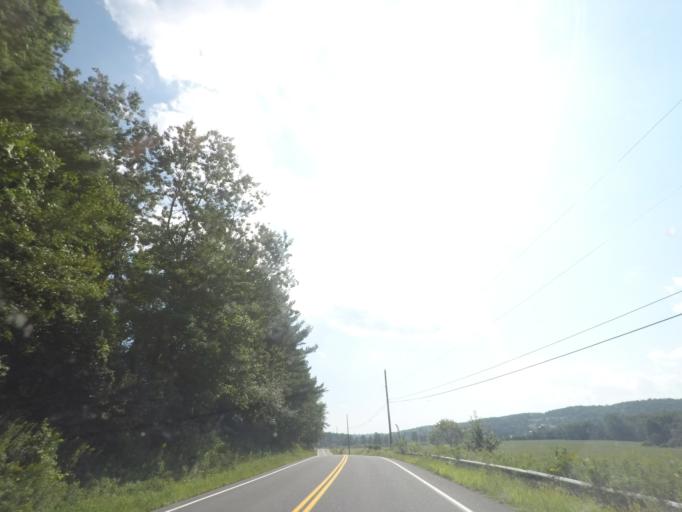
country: US
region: New York
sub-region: Rensselaer County
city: Poestenkill
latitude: 42.7937
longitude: -73.5313
